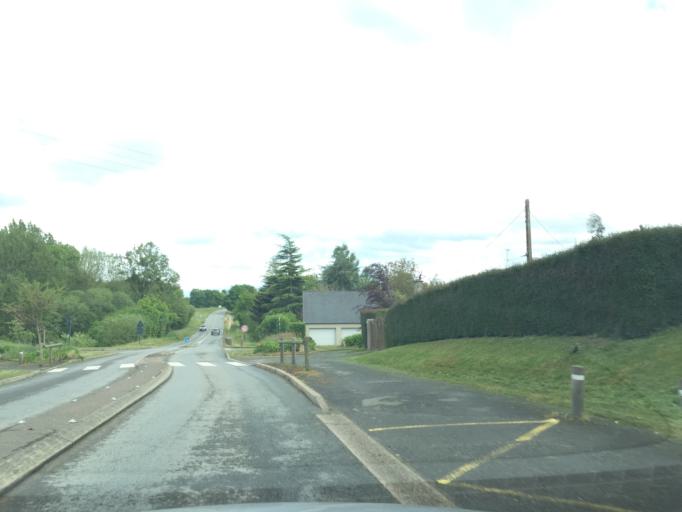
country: FR
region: Brittany
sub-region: Departement des Cotes-d'Armor
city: Ploubalay
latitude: 48.5889
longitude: -2.1457
